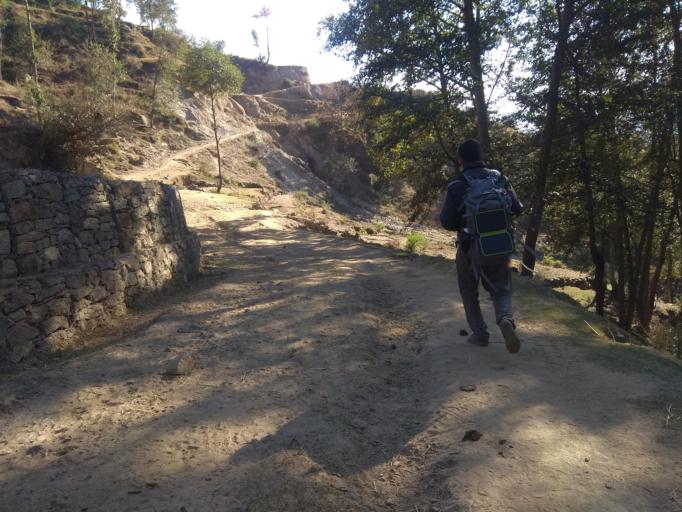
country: NP
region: Far Western
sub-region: Seti Zone
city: Achham
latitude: 29.2543
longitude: 81.6411
